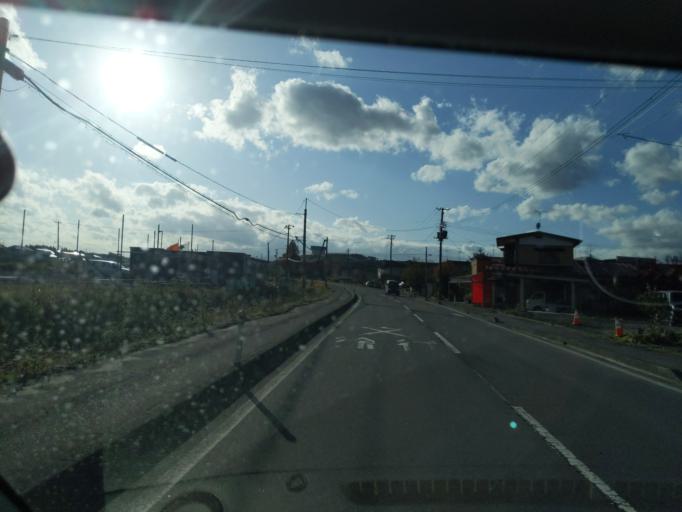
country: JP
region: Iwate
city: Mizusawa
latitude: 39.1238
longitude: 141.1160
